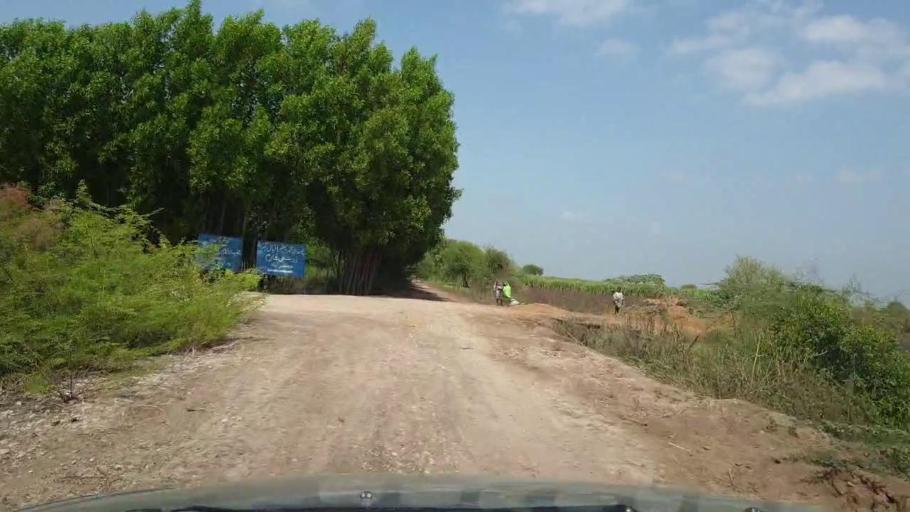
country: PK
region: Sindh
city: Rajo Khanani
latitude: 25.0322
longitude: 68.9165
